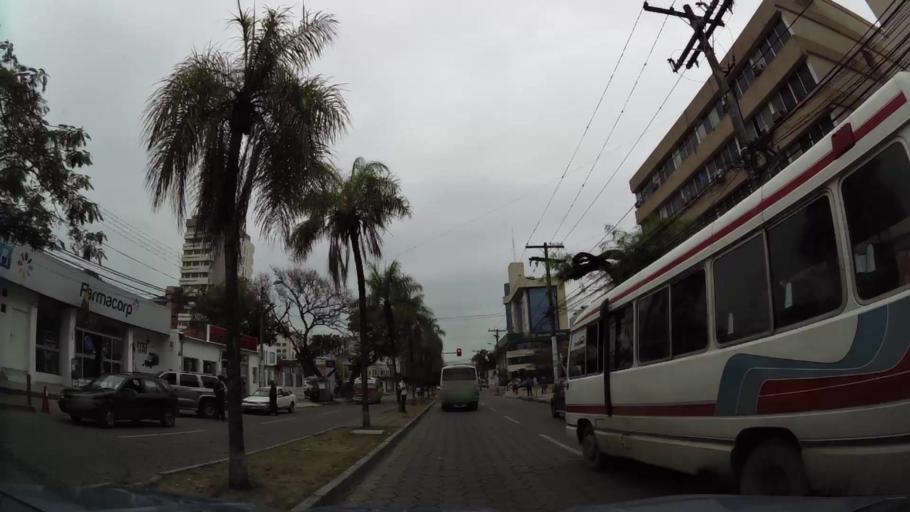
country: BO
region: Santa Cruz
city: Santa Cruz de la Sierra
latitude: -17.7949
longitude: -63.1819
